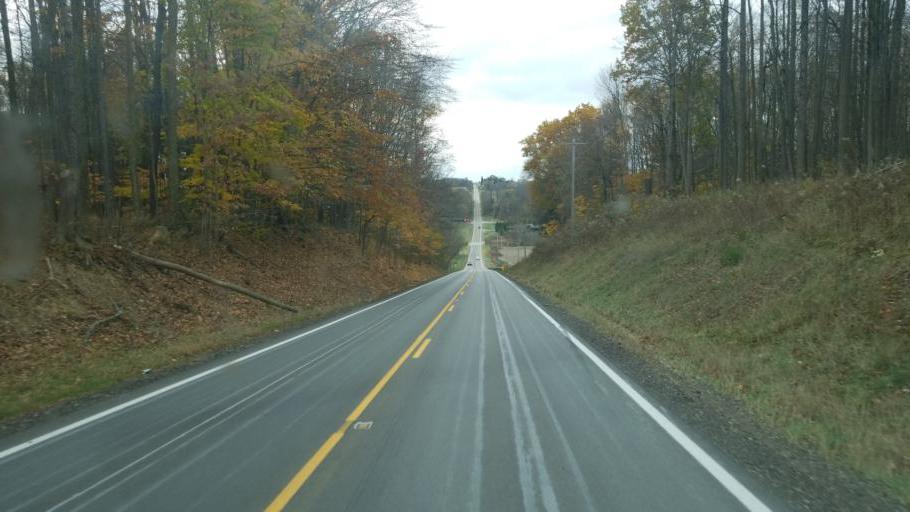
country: US
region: Ohio
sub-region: Richland County
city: Ontario
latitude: 40.7117
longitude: -82.6659
